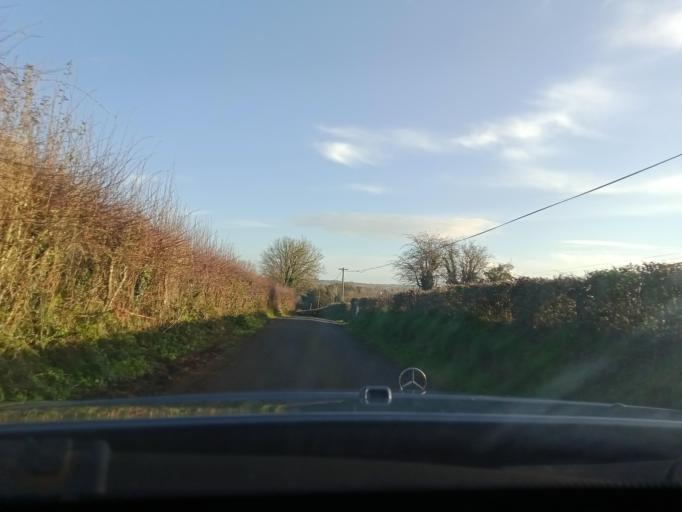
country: IE
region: Munster
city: Carrick-on-Suir
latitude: 52.4369
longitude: -7.4123
